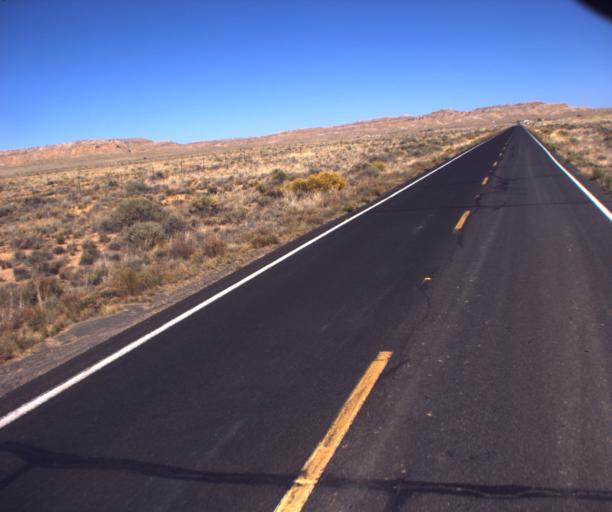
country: US
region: Arizona
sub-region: Navajo County
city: First Mesa
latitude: 35.7626
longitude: -110.5098
